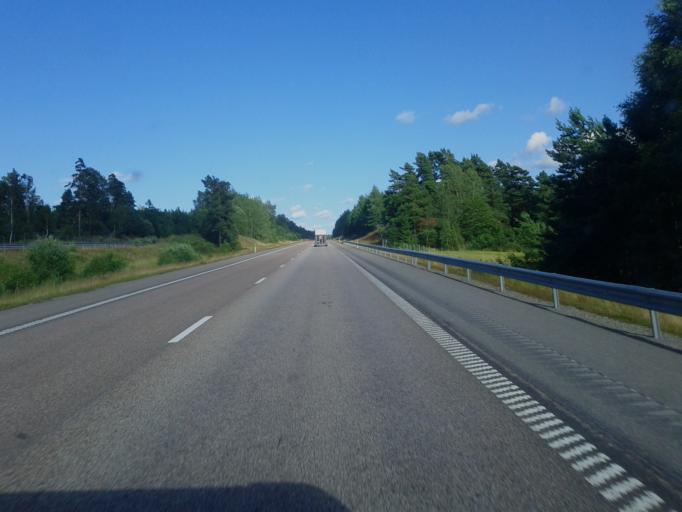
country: SE
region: Uppsala
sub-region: Enkopings Kommun
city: Grillby
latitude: 59.6325
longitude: 17.3012
